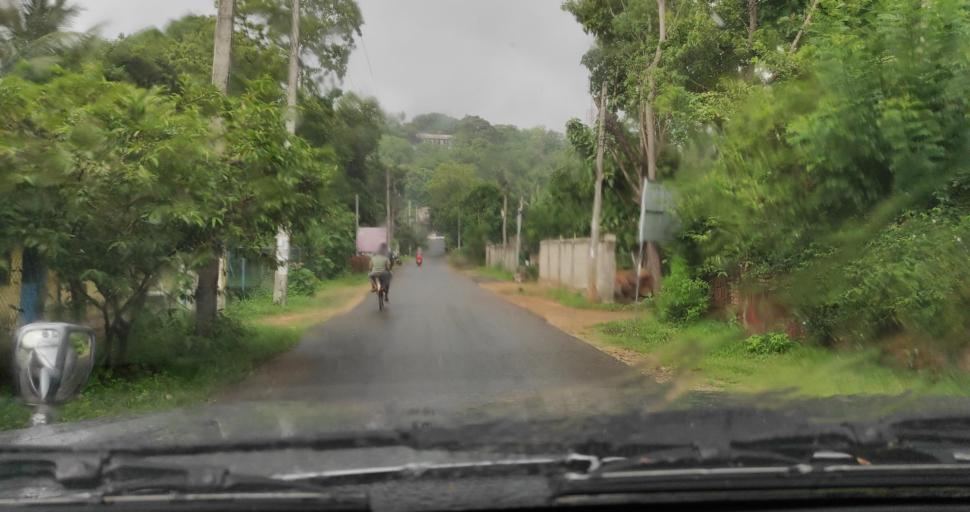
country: LK
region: Eastern Province
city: Trincomalee
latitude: 8.3679
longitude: 81.0059
